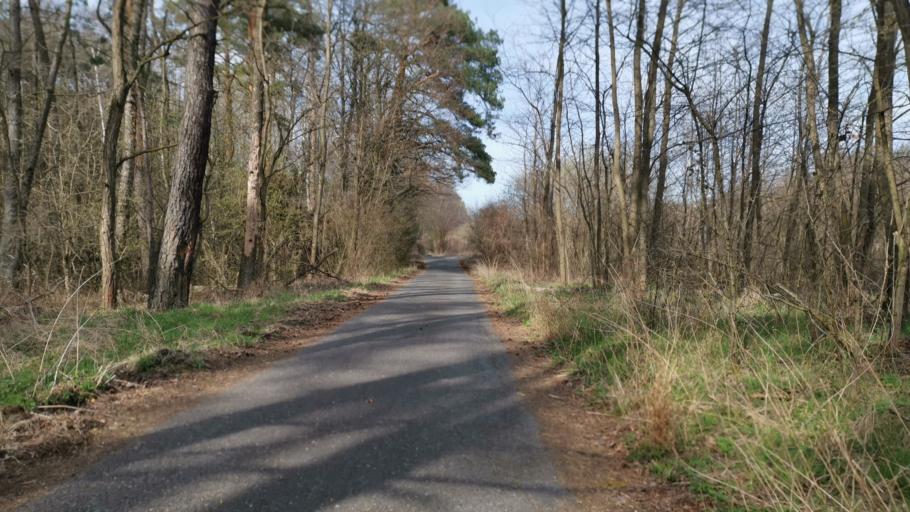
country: SK
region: Trnavsky
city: Gbely
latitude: 48.6758
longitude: 17.0571
